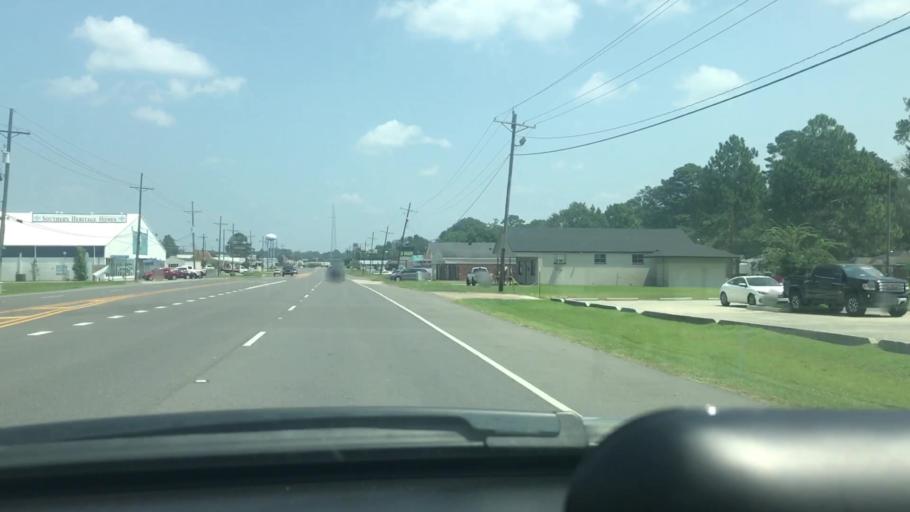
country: US
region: Louisiana
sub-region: Livingston Parish
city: Denham Springs
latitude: 30.4766
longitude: -90.9602
